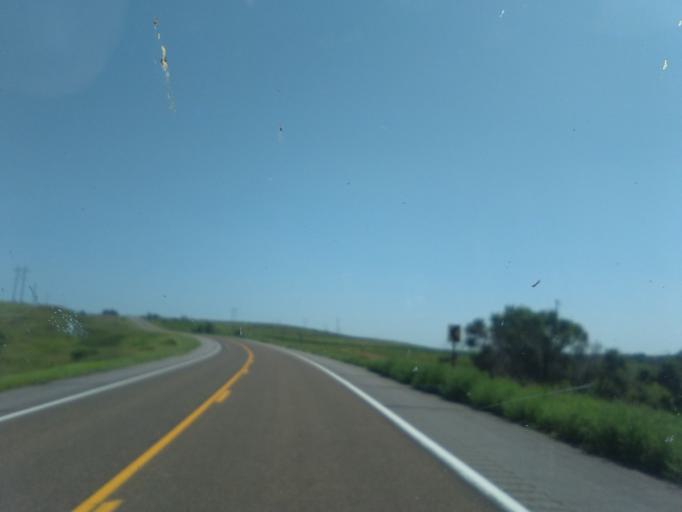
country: US
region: Nebraska
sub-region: Hitchcock County
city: Trenton
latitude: 40.1615
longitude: -101.1605
